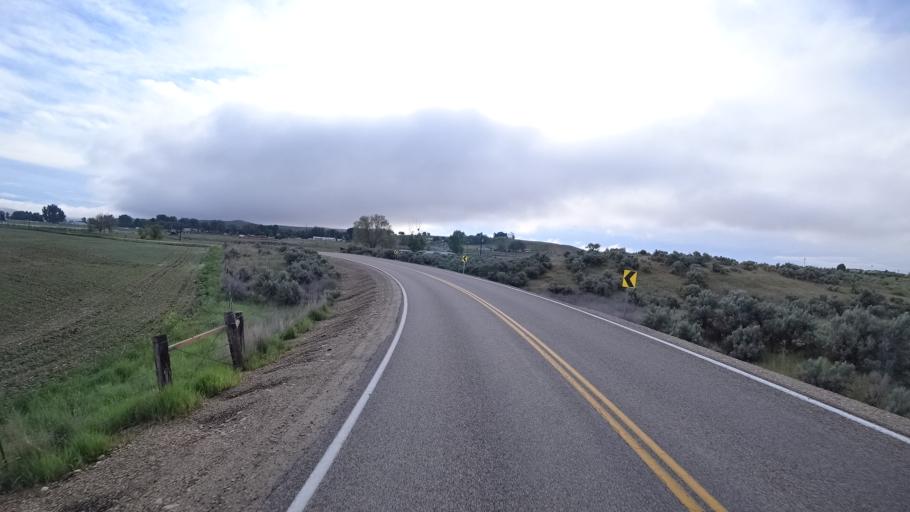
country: US
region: Idaho
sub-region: Ada County
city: Star
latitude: 43.7719
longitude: -116.4743
